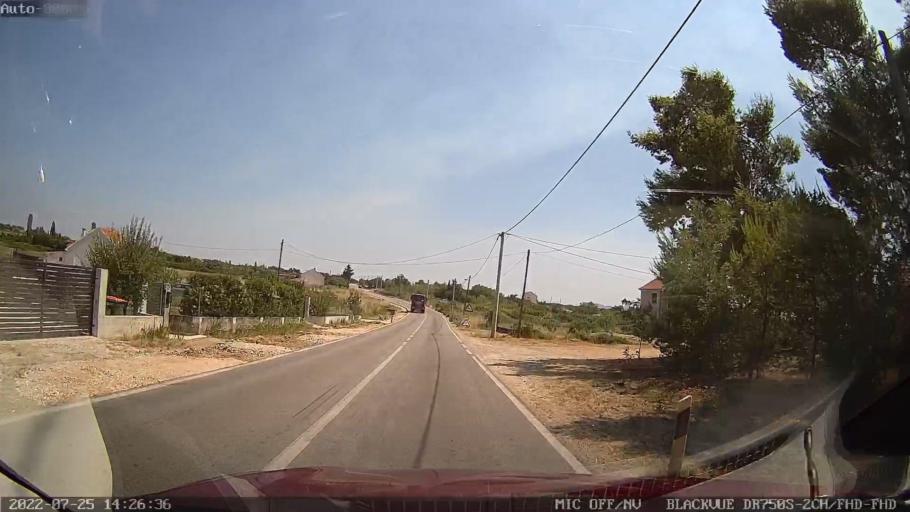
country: HR
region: Zadarska
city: Policnik
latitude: 44.1379
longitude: 15.3392
